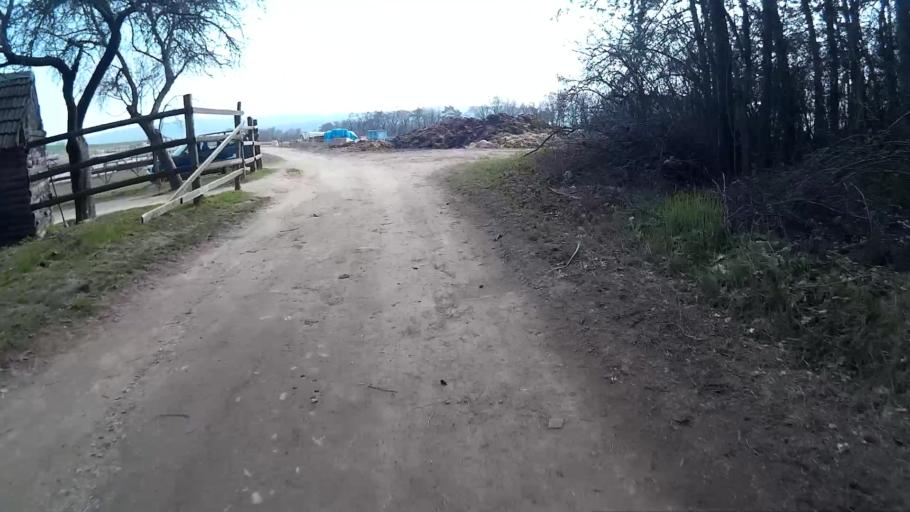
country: CZ
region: South Moravian
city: Bilovice nad Svitavou
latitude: 49.2450
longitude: 16.6404
